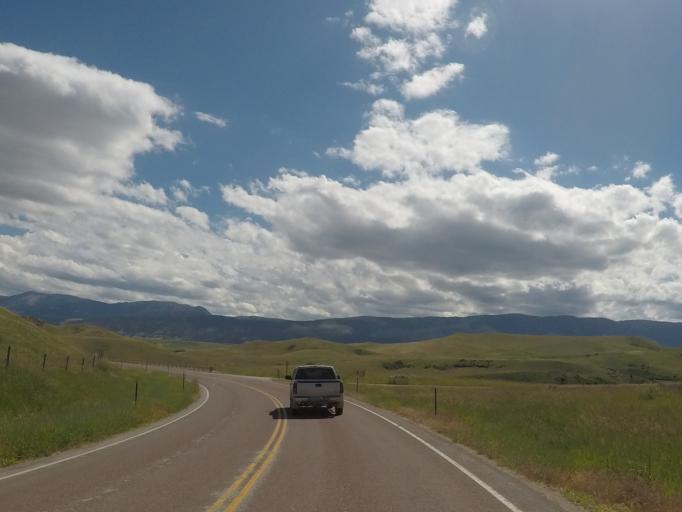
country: US
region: Wyoming
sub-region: Sheridan County
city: Sheridan
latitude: 44.9190
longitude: -107.3013
